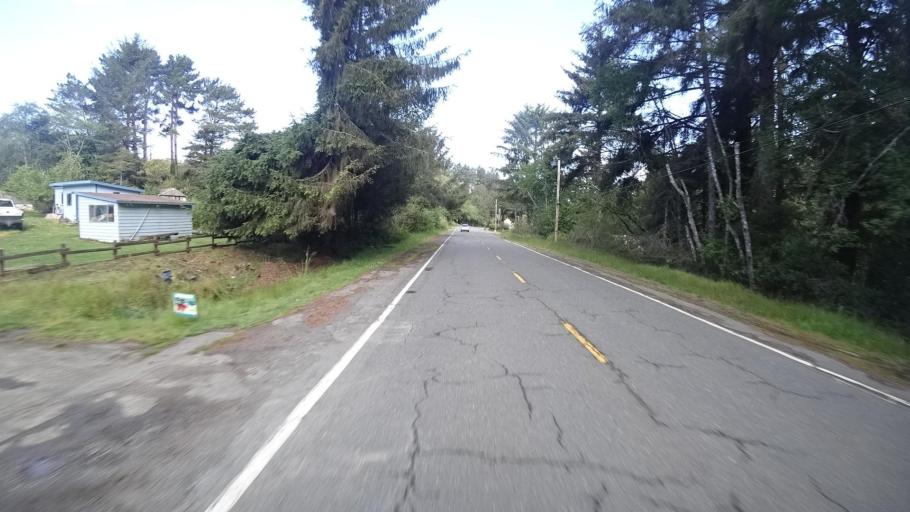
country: US
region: California
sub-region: Humboldt County
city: McKinleyville
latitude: 40.9872
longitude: -124.1081
